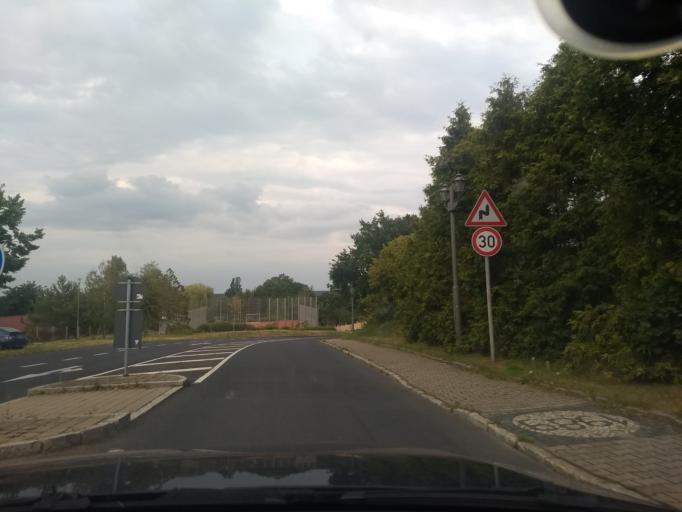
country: DE
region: Saxony
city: Radeburg
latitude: 51.2128
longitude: 13.7164
